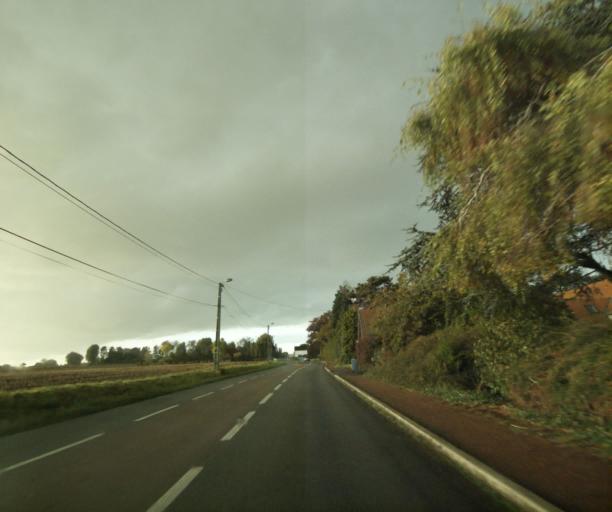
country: FR
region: Nord-Pas-de-Calais
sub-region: Departement du Nord
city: Linselles
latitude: 50.7509
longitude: 3.0955
